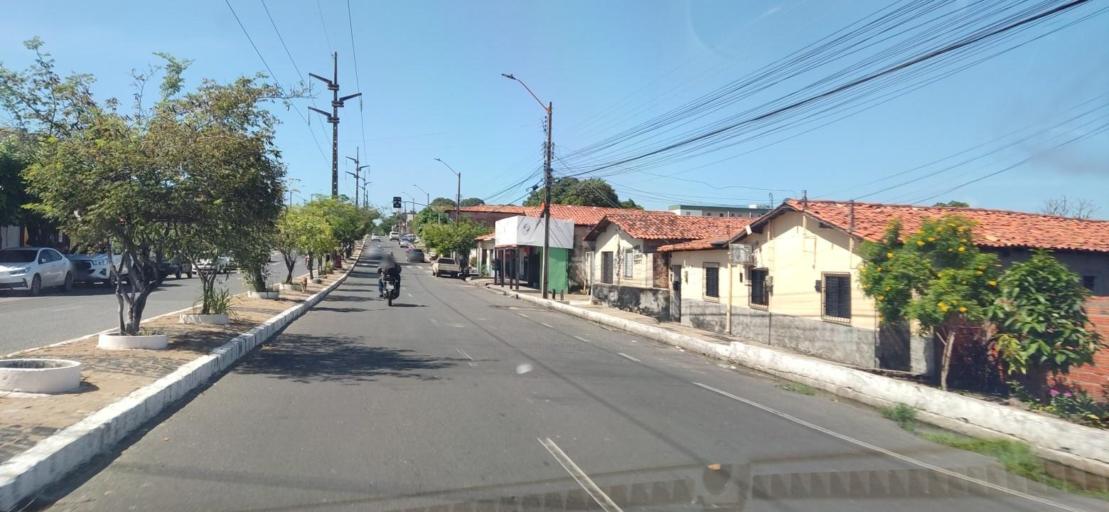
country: BR
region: Piaui
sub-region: Teresina
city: Teresina
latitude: -5.1192
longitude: -42.8099
